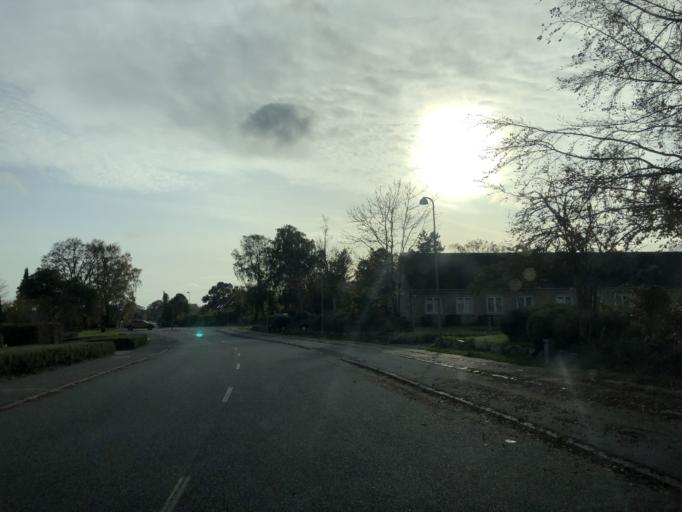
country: DK
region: Capital Region
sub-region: Rudersdal Kommune
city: Holte
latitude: 55.7898
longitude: 12.4627
